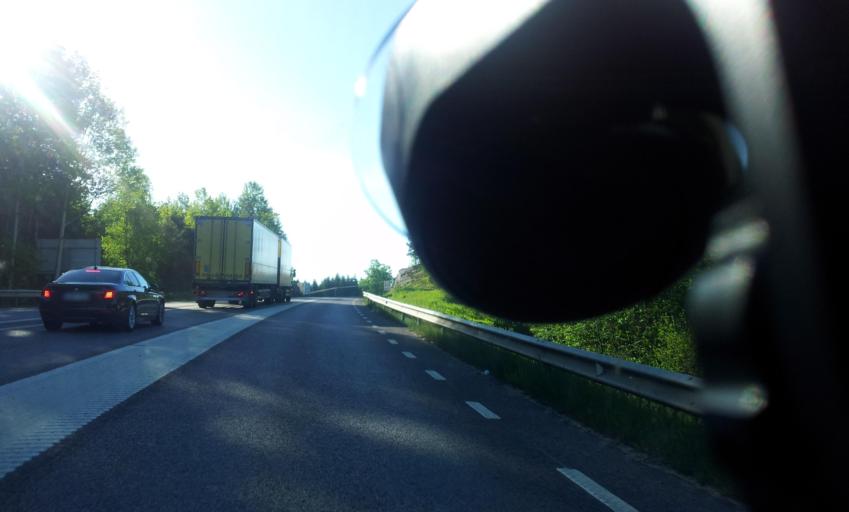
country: SE
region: Kalmar
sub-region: Vasterviks Kommun
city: Ankarsrum
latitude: 57.7222
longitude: 16.4562
